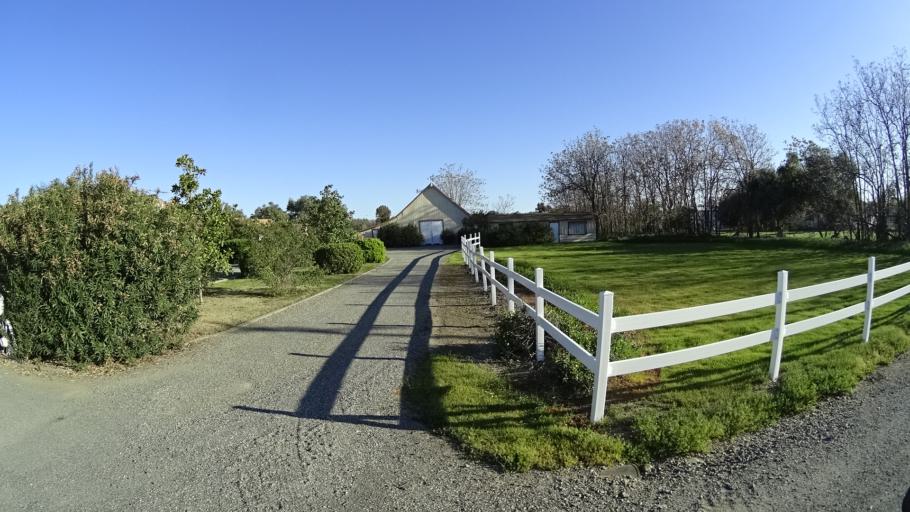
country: US
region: California
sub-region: Glenn County
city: Orland
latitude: 39.7547
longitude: -122.2081
